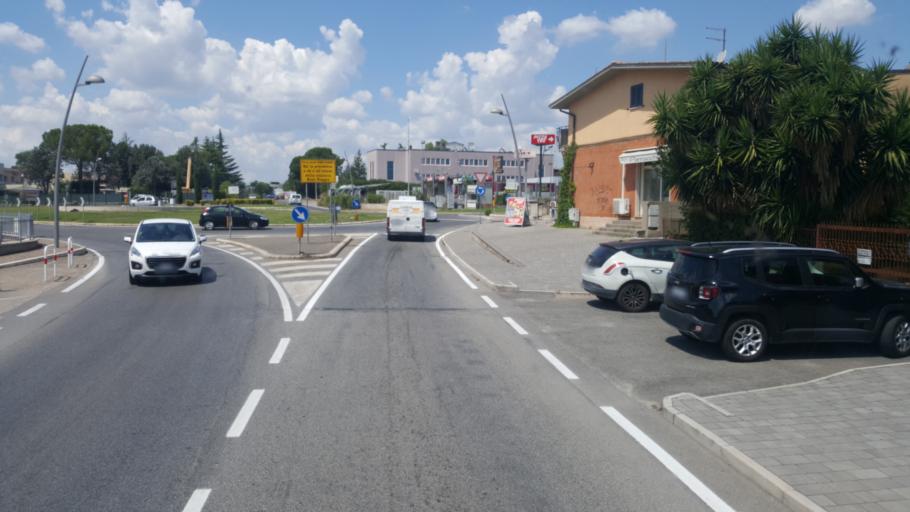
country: IT
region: Latium
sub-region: Citta metropolitana di Roma Capitale
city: Fiano Romano
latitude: 42.1404
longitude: 12.5971
